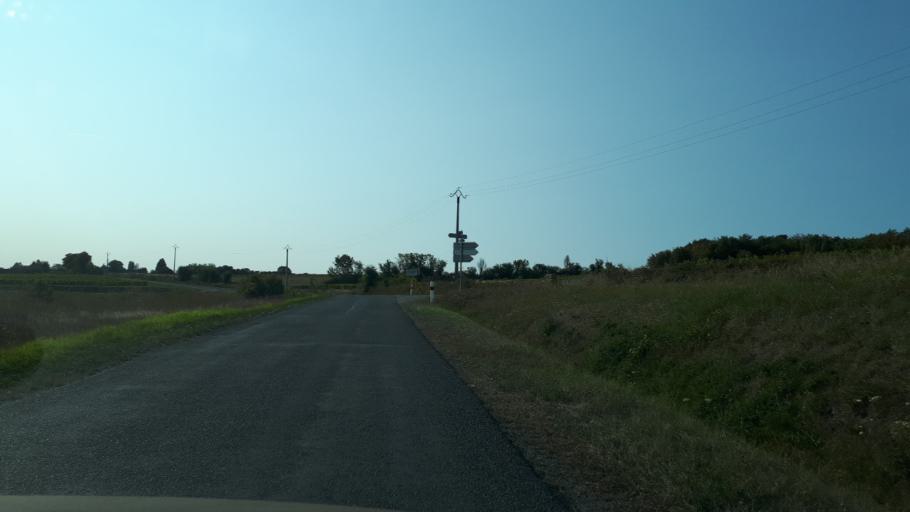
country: FR
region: Centre
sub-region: Departement du Cher
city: Menetou-Salon
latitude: 47.2312
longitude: 2.5144
